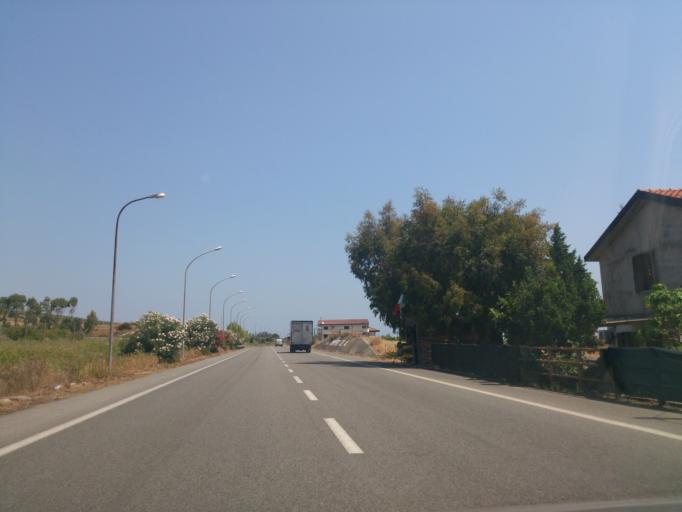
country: IT
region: Calabria
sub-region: Provincia di Reggio Calabria
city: Riace Marina
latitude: 38.4020
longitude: 16.5438
